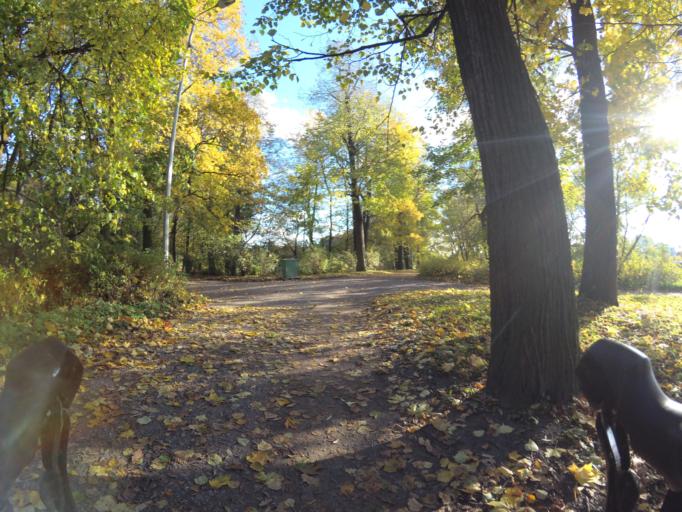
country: RU
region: St.-Petersburg
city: Staraya Derevnya
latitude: 59.9795
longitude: 30.2464
